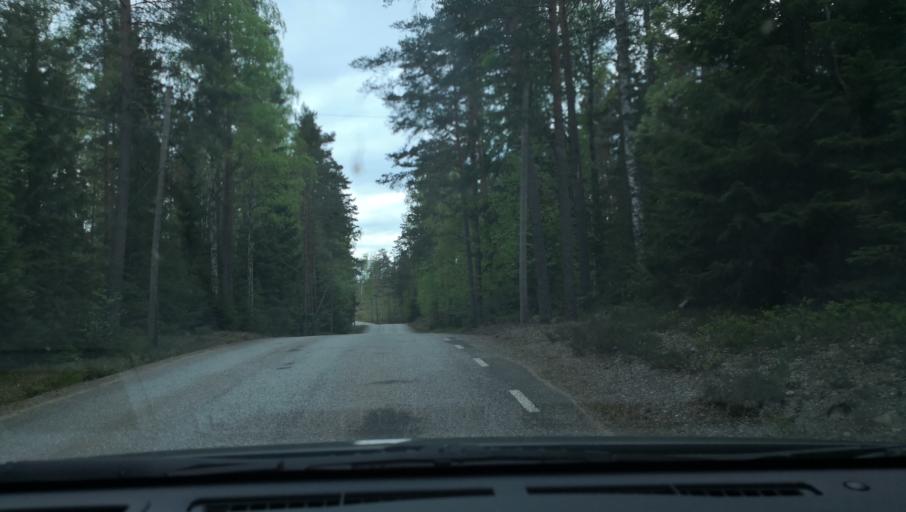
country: SE
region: Vaestmanland
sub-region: Skinnskattebergs Kommun
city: Skinnskatteberg
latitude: 59.8253
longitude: 15.5522
